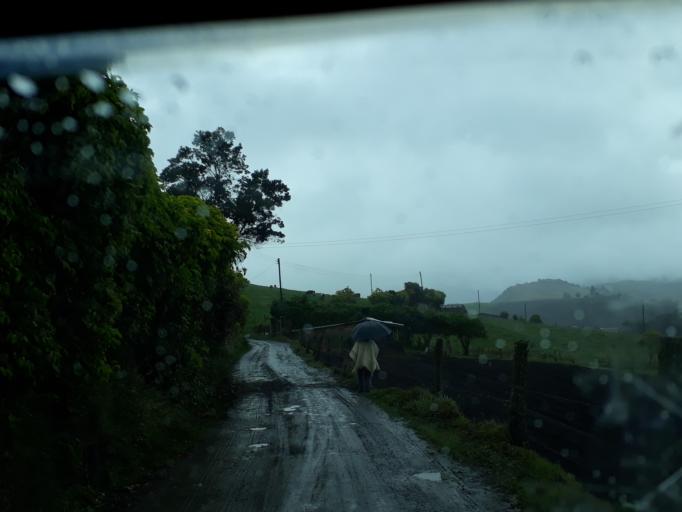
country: CO
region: Cundinamarca
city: La Mesa
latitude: 5.1692
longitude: -73.9138
